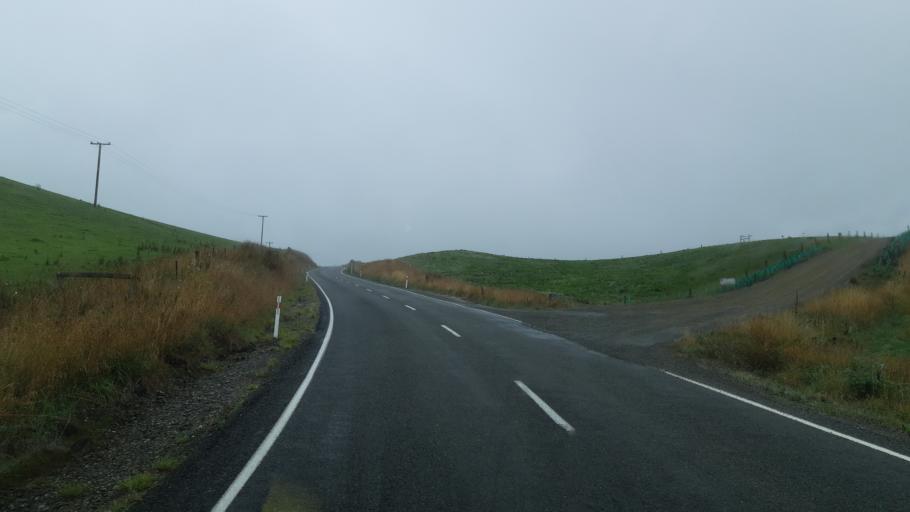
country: NZ
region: Otago
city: Oamaru
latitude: -44.9125
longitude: 170.8366
